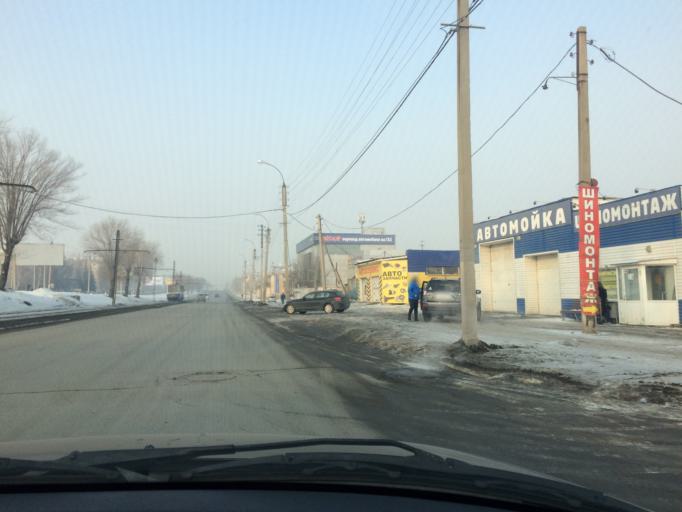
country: RU
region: Chelyabinsk
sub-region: Gorod Magnitogorsk
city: Magnitogorsk
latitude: 53.4206
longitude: 58.9618
